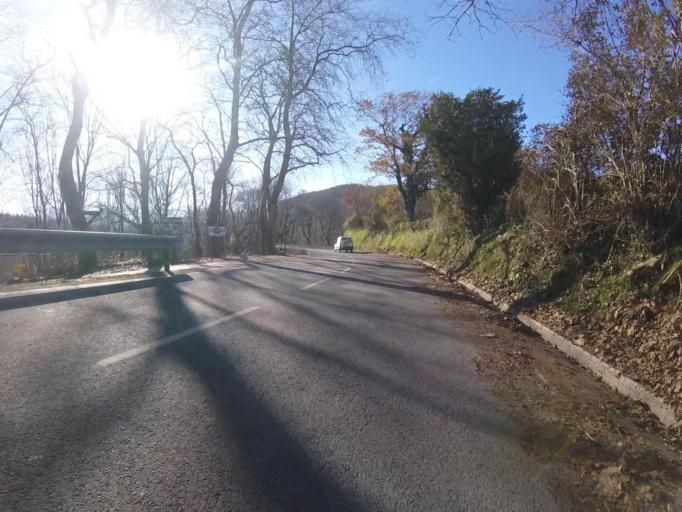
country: ES
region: Navarre
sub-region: Provincia de Navarra
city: Bera
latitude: 43.3091
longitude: -1.6845
